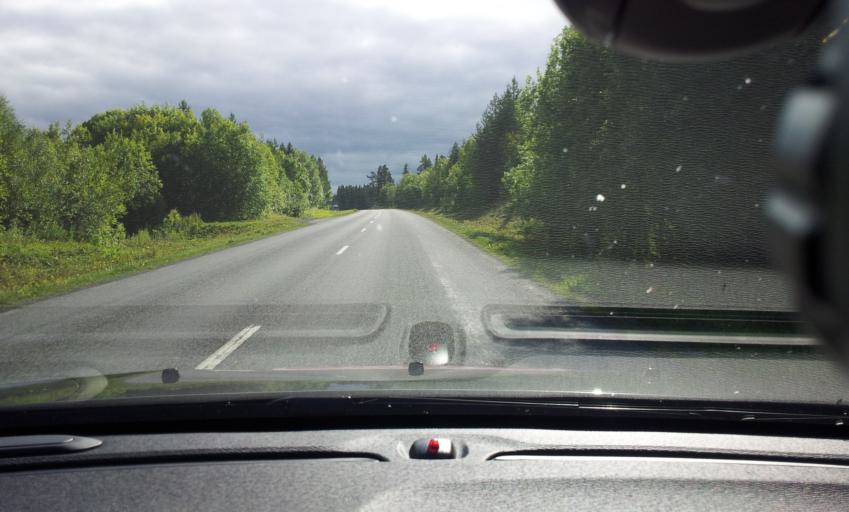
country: SE
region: Jaemtland
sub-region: Krokoms Kommun
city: Krokom
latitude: 63.4648
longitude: 14.1936
